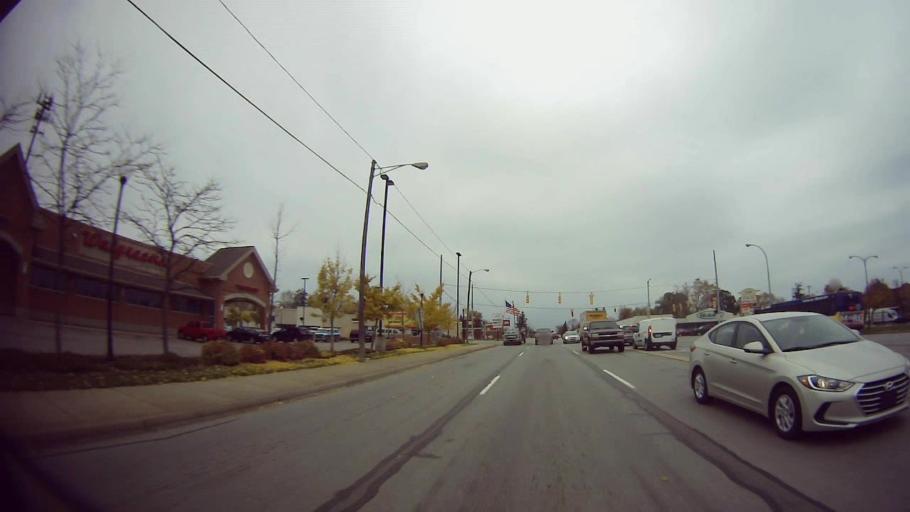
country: US
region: Michigan
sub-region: Oakland County
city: Sylvan Lake
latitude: 42.6348
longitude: -83.3257
